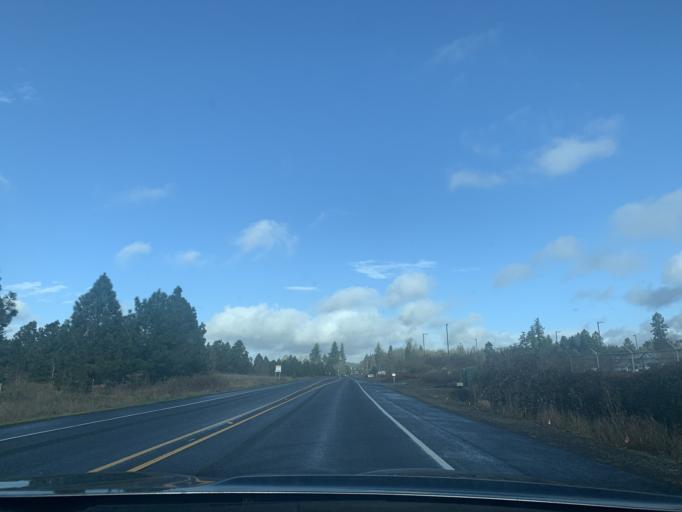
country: US
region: Oregon
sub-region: Washington County
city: Sherwood
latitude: 45.3961
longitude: -122.8519
